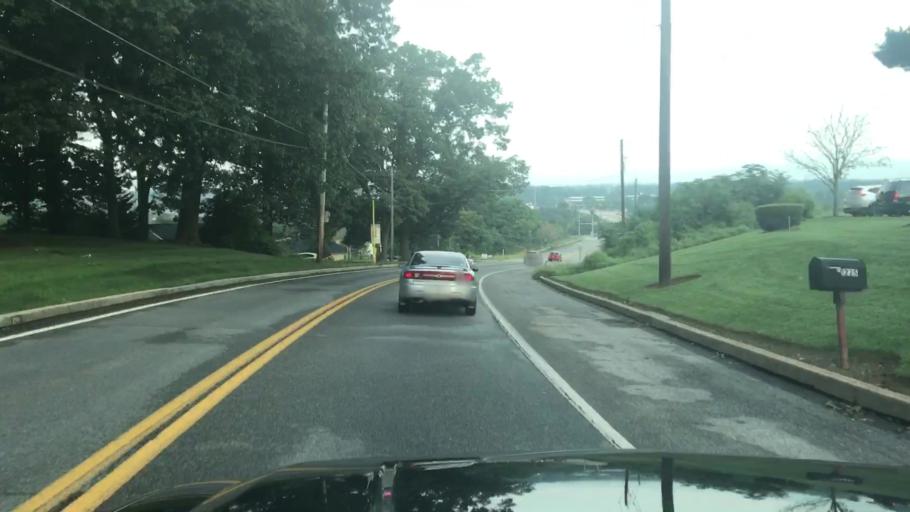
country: US
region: Pennsylvania
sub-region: Cumberland County
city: Shiremanstown
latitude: 40.2022
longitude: -76.9527
